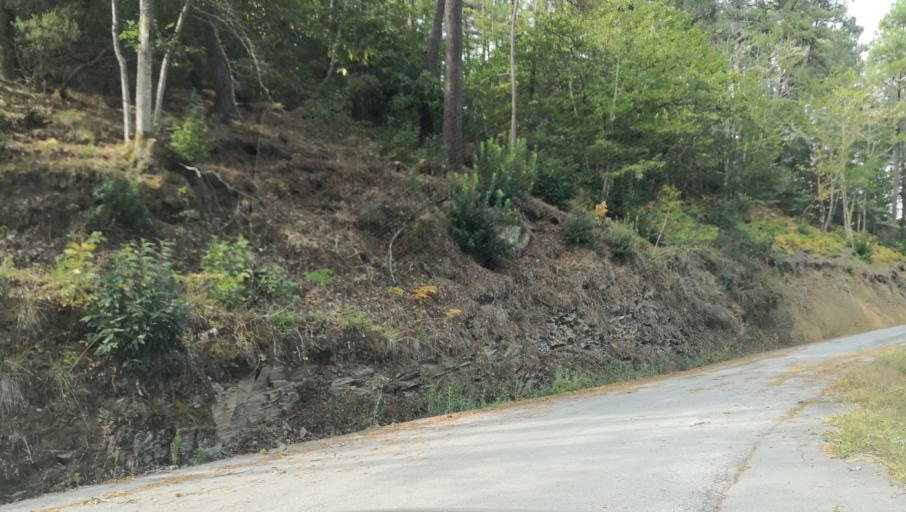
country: PT
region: Vila Real
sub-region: Sabrosa
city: Vilela
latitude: 41.2280
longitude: -7.6832
